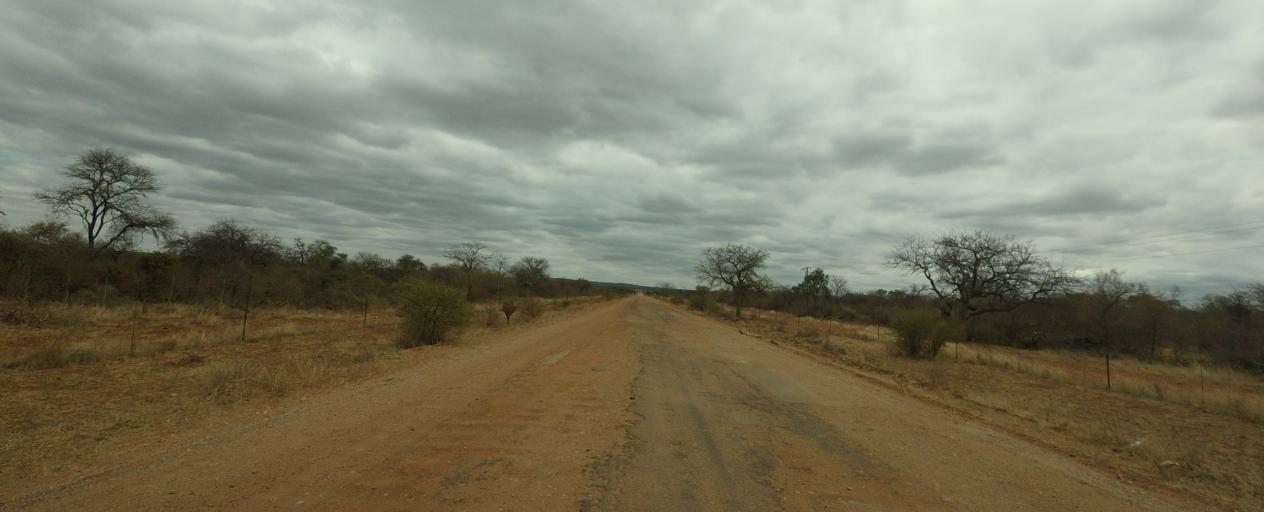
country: BW
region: Central
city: Mathathane
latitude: -22.7400
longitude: 28.4859
